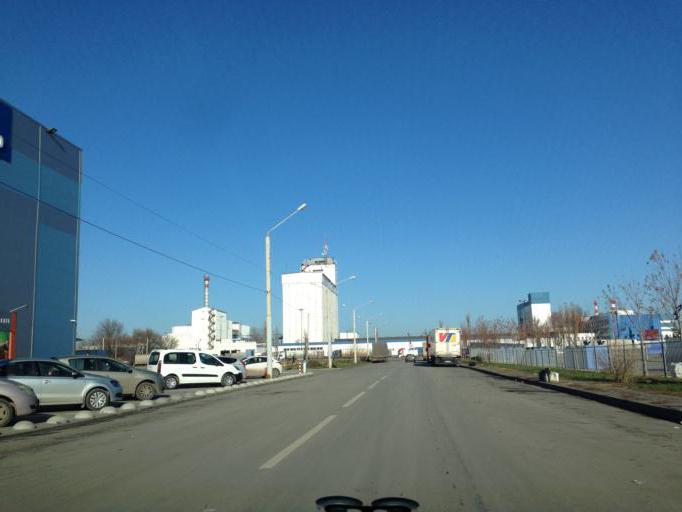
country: RU
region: Rostov
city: Kalinin
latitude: 47.2358
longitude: 39.6052
